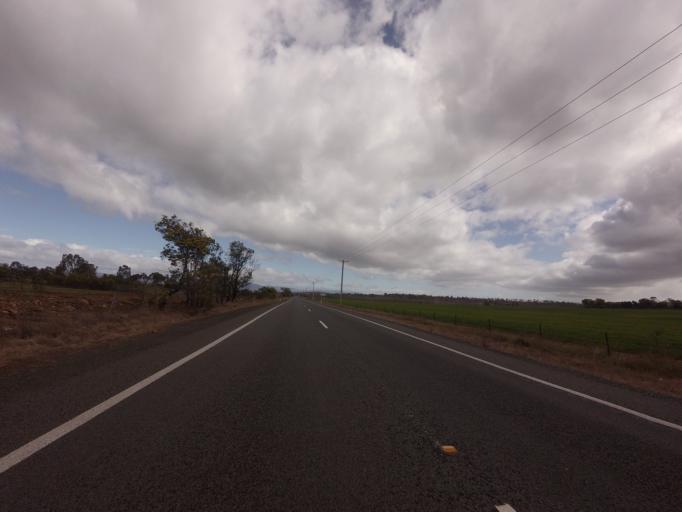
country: AU
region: Tasmania
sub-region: Northern Midlands
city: Evandale
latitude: -41.8342
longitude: 147.4616
